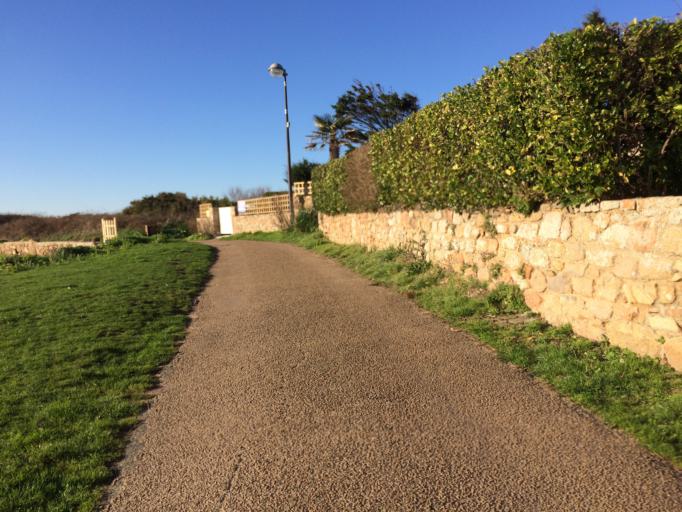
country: FR
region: Brittany
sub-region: Departement des Cotes-d'Armor
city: Ploubazlanec
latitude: 48.8626
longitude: -2.9939
